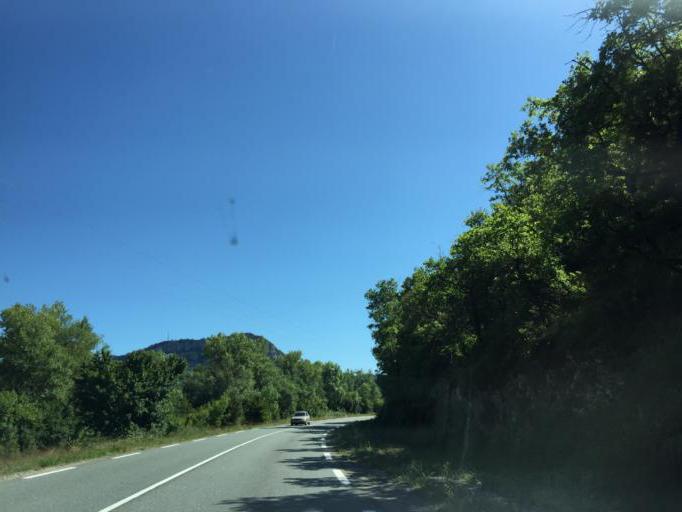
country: FR
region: Midi-Pyrenees
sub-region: Departement de l'Aveyron
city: Saint-Georges-de-Luzencon
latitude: 43.9993
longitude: 2.9694
